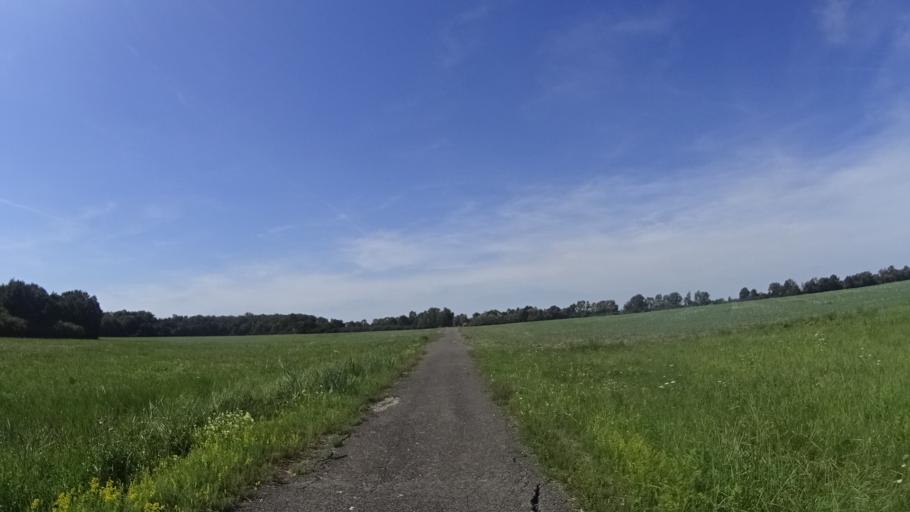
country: AT
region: Lower Austria
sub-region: Politischer Bezirk Ganserndorf
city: Angern an der March
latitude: 48.3585
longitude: 16.8781
